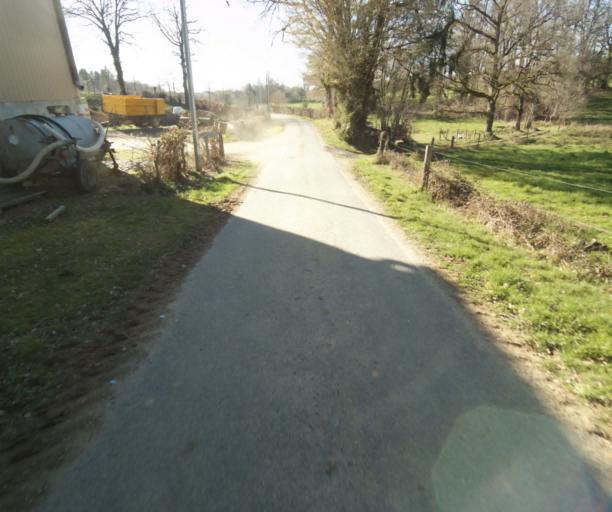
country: FR
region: Limousin
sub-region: Departement de la Correze
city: Seilhac
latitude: 45.3927
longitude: 1.6758
